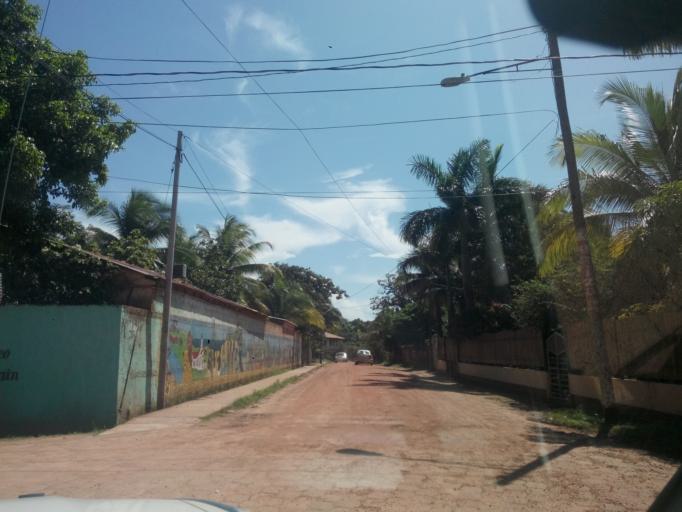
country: NI
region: Atlantico Norte (RAAN)
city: Puerto Cabezas
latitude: 14.0361
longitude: -83.3808
